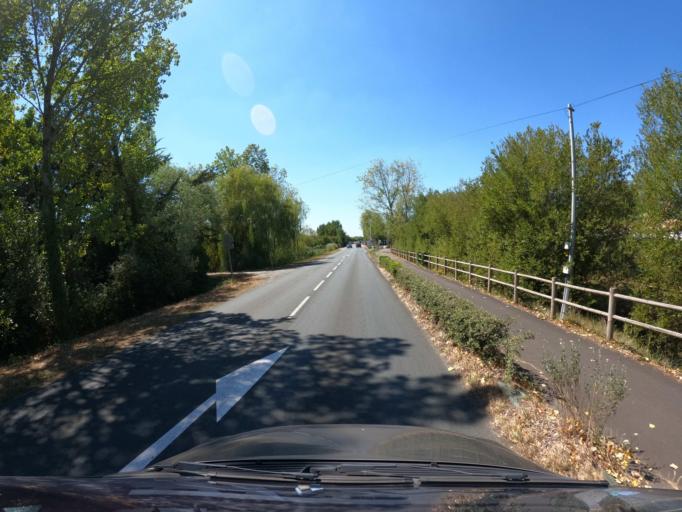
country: FR
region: Pays de la Loire
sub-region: Departement de la Vendee
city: Le Perrier
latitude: 46.8200
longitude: -1.9884
